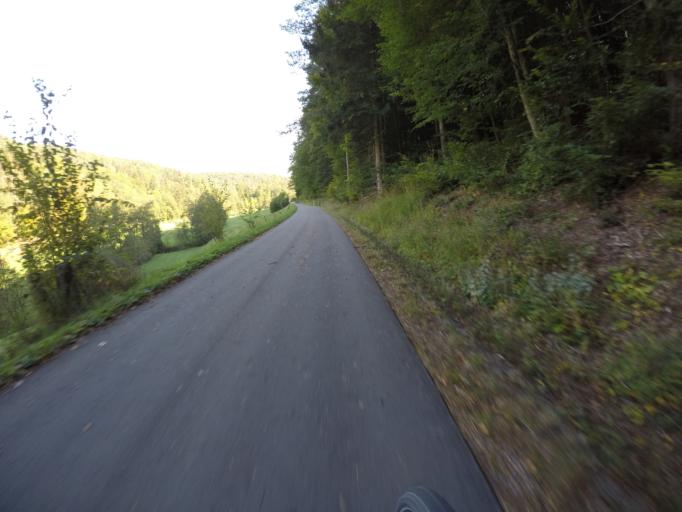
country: DE
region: Baden-Wuerttemberg
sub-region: Regierungsbezirk Stuttgart
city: Waldenbuch
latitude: 48.6460
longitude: 9.1624
